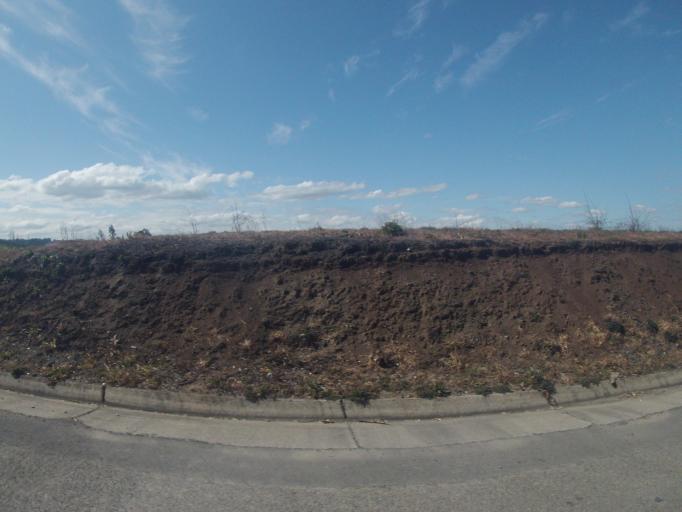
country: CL
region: Biobio
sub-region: Provincia de Biobio
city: Los Angeles
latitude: -37.4526
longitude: -72.4086
